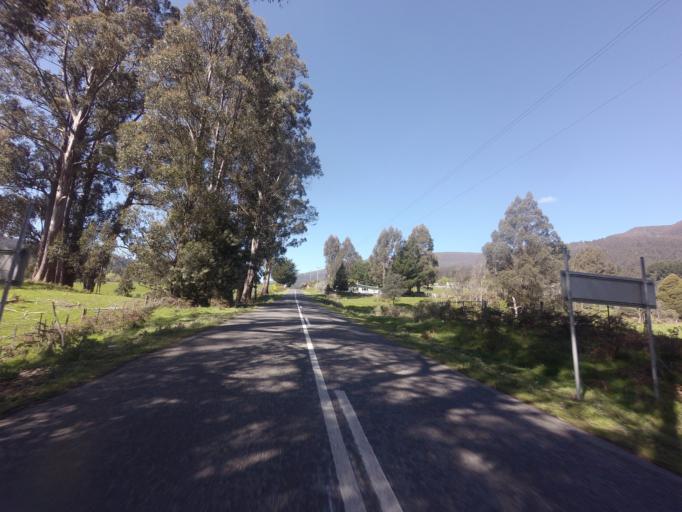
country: AU
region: Tasmania
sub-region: Derwent Valley
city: New Norfolk
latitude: -42.7572
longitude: 146.6205
